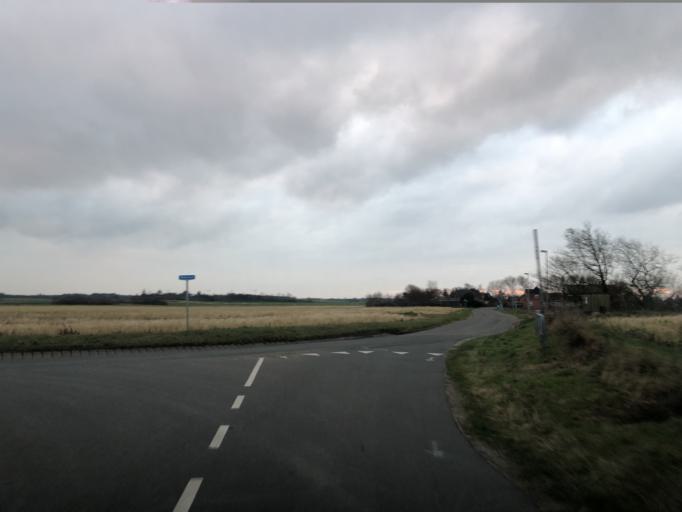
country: DK
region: Central Jutland
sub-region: Holstebro Kommune
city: Ulfborg
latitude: 56.2386
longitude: 8.2846
